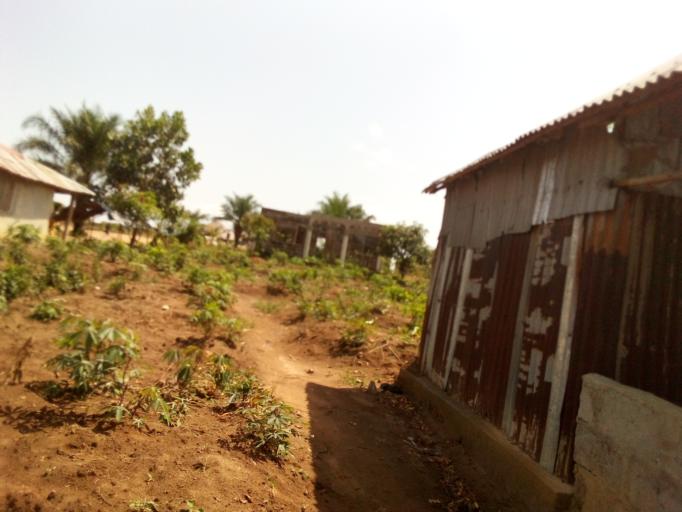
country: SL
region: Western Area
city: Waterloo
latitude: 8.3430
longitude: -13.0193
